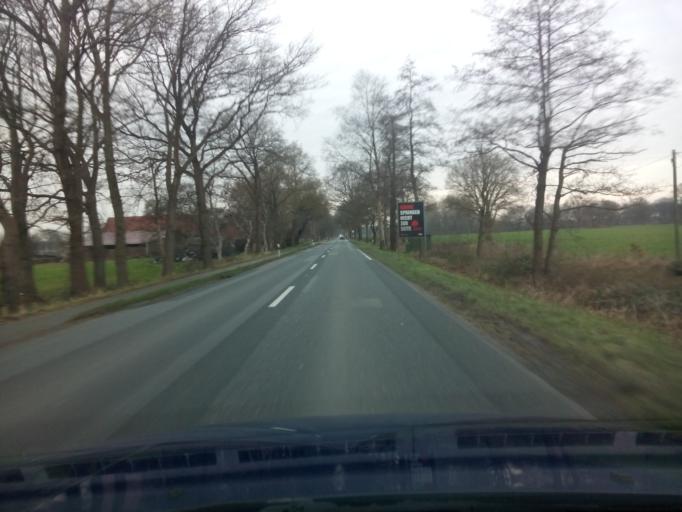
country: DE
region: Lower Saxony
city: Flogeln
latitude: 53.6239
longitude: 8.8109
